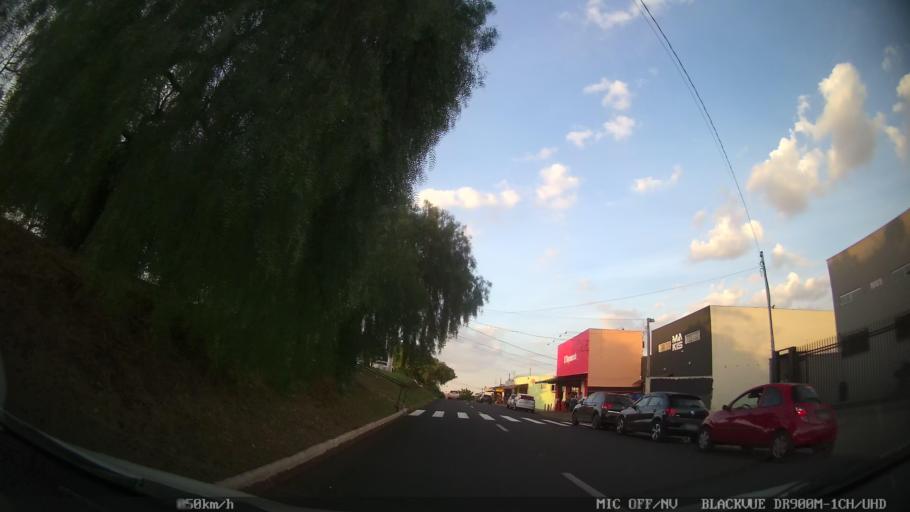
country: BR
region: Sao Paulo
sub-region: Ribeirao Preto
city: Ribeirao Preto
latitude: -21.1373
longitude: -47.8491
